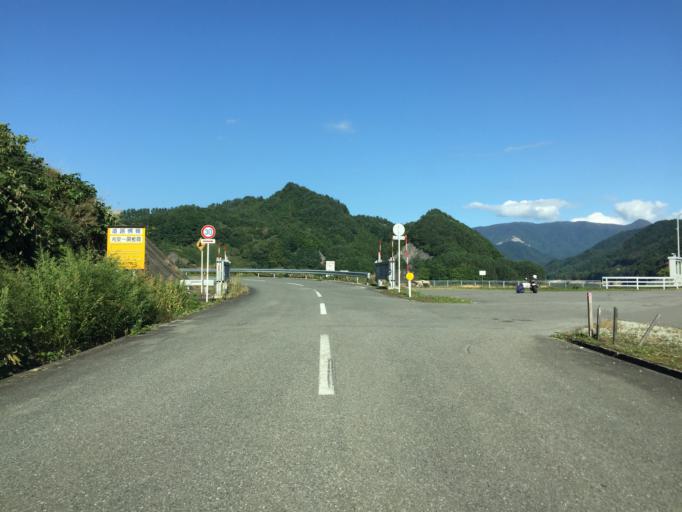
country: JP
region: Yamagata
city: Yonezawa
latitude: 37.8639
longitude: 140.1665
